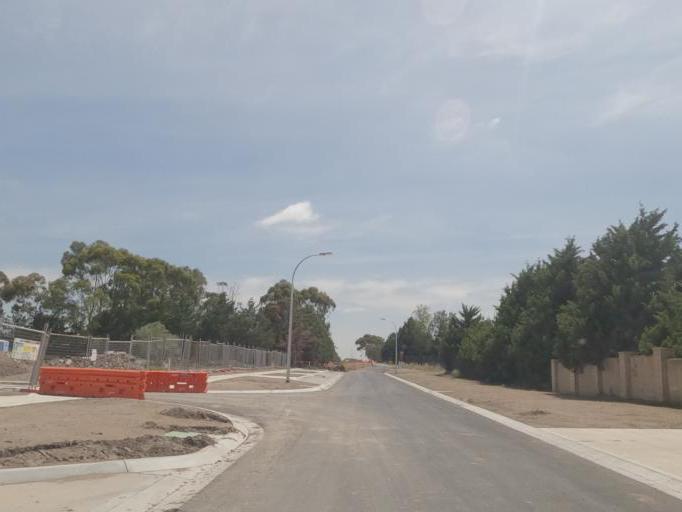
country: AU
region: Victoria
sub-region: Hume
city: Greenvale
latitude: -37.6413
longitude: 144.8746
